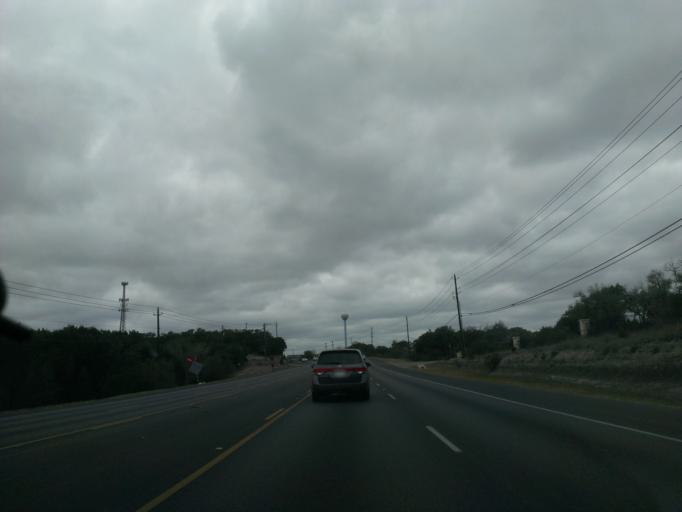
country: US
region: Texas
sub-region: Travis County
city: Lakeway
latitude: 30.3590
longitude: -97.9552
